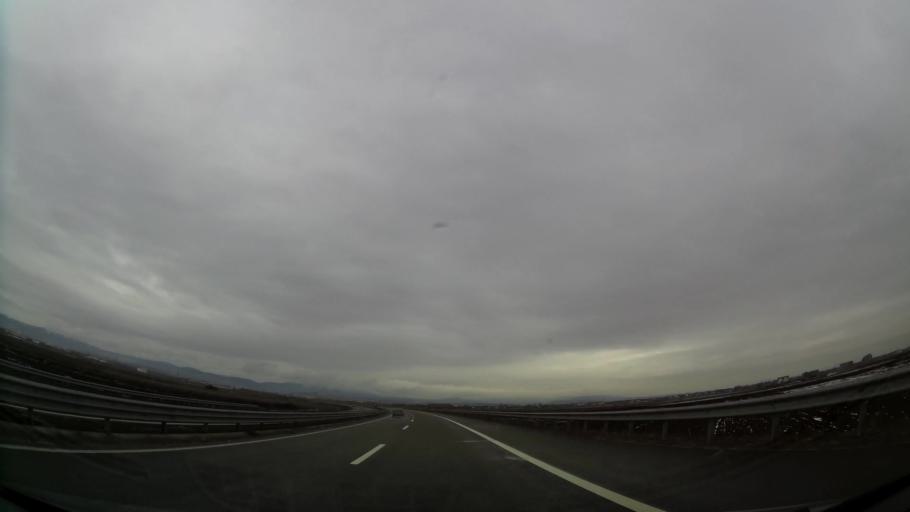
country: XK
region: Pristina
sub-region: Lipjan
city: Lipljan
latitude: 42.5316
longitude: 21.1411
